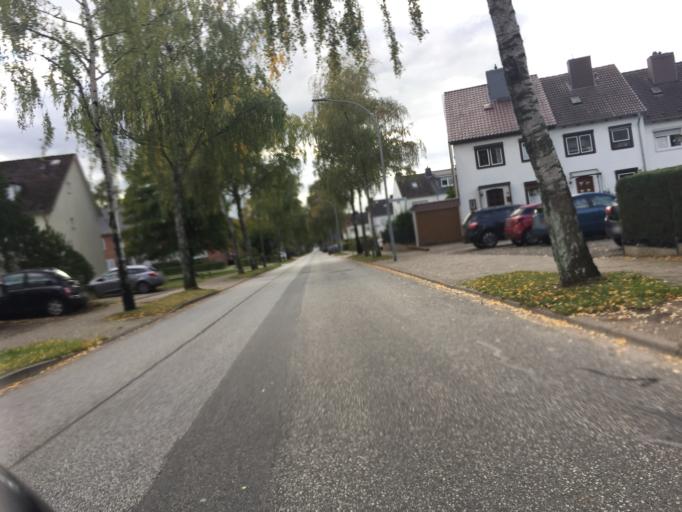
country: DE
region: Schleswig-Holstein
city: Itzehoe
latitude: 53.9403
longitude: 9.5069
